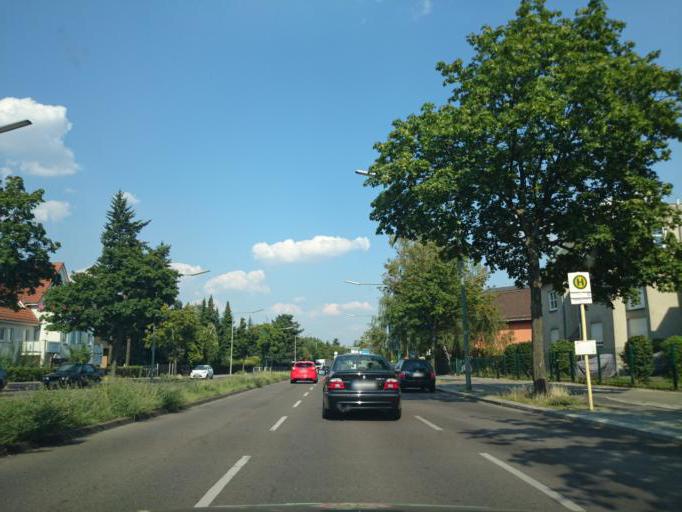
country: DE
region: Berlin
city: Buckow
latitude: 52.4332
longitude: 13.4647
